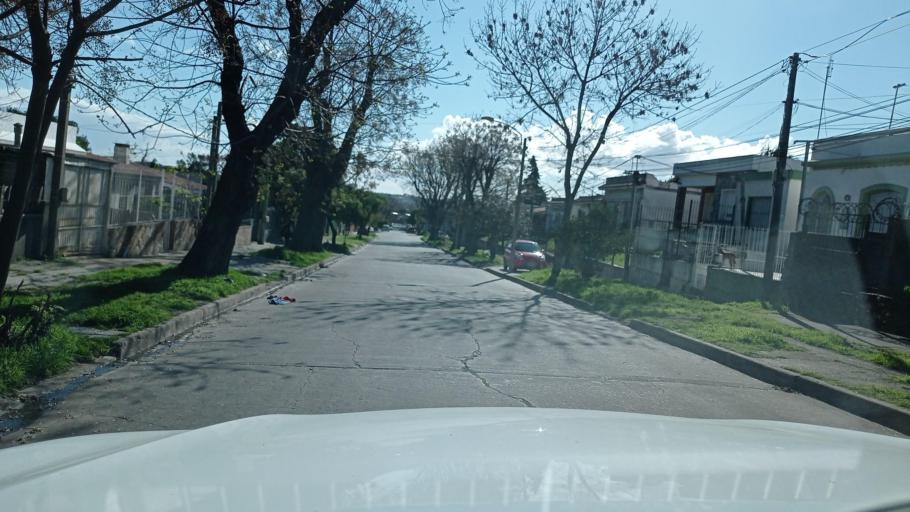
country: UY
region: Montevideo
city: Montevideo
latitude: -34.8515
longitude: -56.1759
